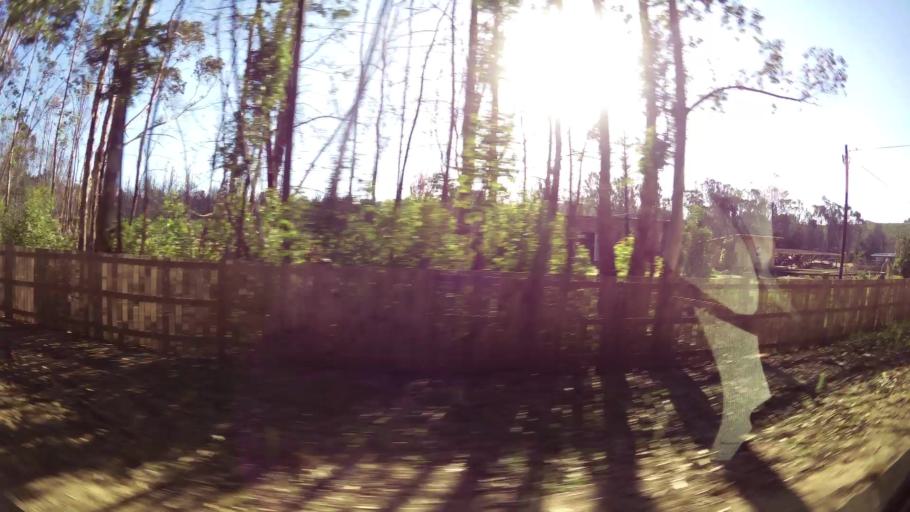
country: ZA
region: Western Cape
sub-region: Eden District Municipality
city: Knysna
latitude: -34.0293
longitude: 23.0104
